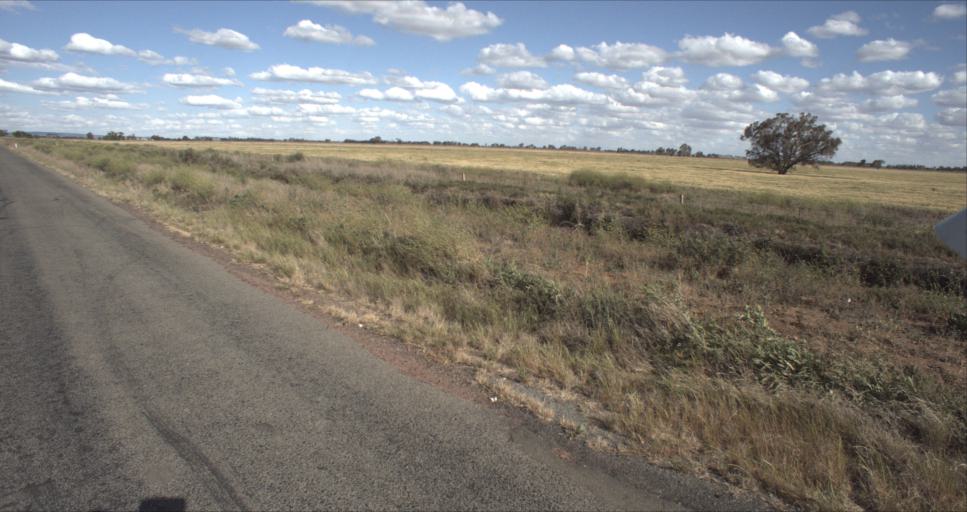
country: AU
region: New South Wales
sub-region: Leeton
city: Leeton
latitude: -34.4429
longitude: 146.2453
